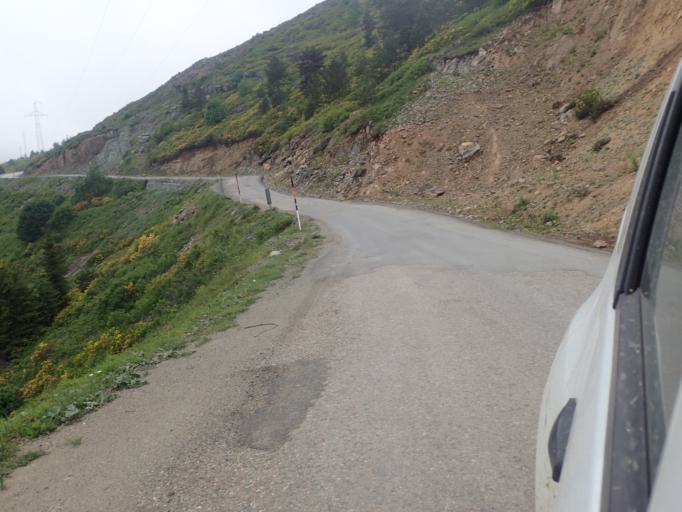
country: TR
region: Ordu
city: Topcam
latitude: 40.6529
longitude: 37.9416
